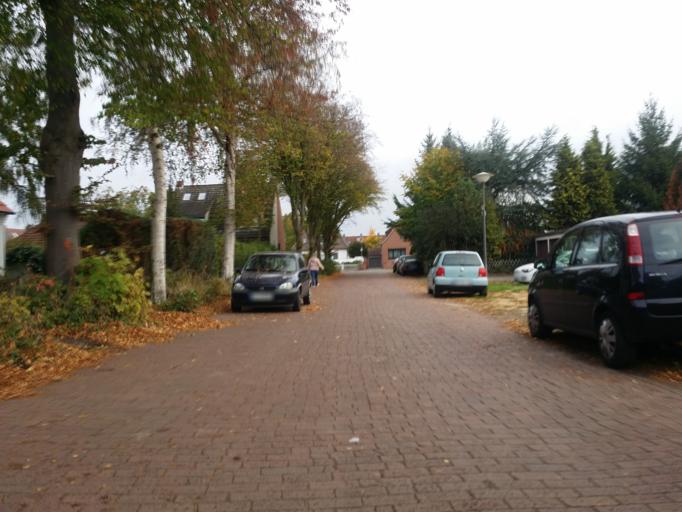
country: DE
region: Lower Saxony
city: Stuhr
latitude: 53.0437
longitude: 8.7385
